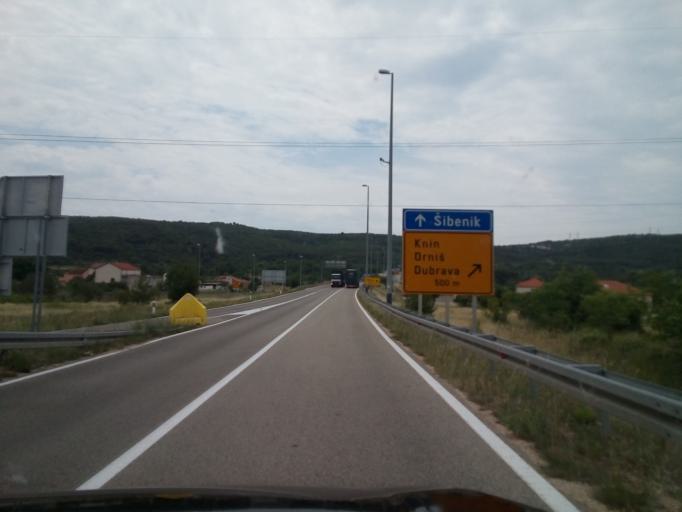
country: HR
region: Sibensko-Kniniska
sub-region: Grad Sibenik
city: Sibenik
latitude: 43.7398
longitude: 15.9382
